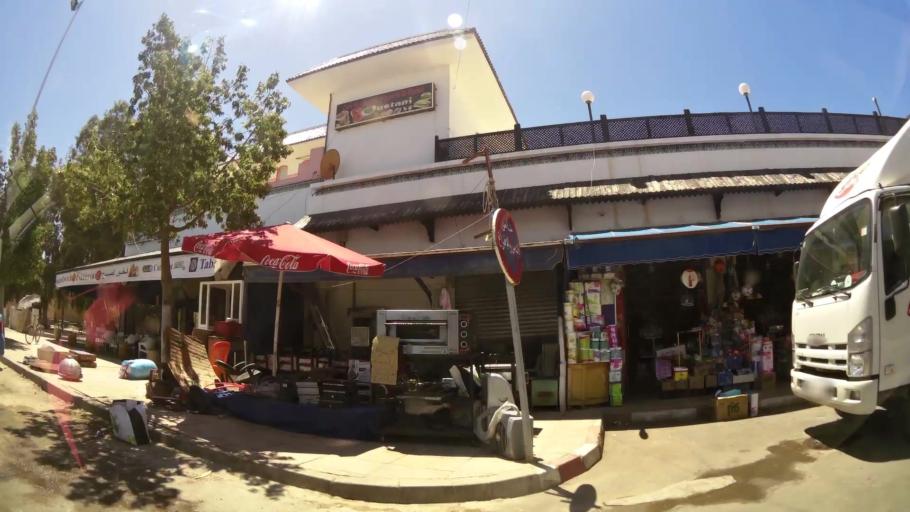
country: MA
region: Oriental
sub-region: Berkane-Taourirt
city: Madagh
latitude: 35.0810
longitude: -2.2147
